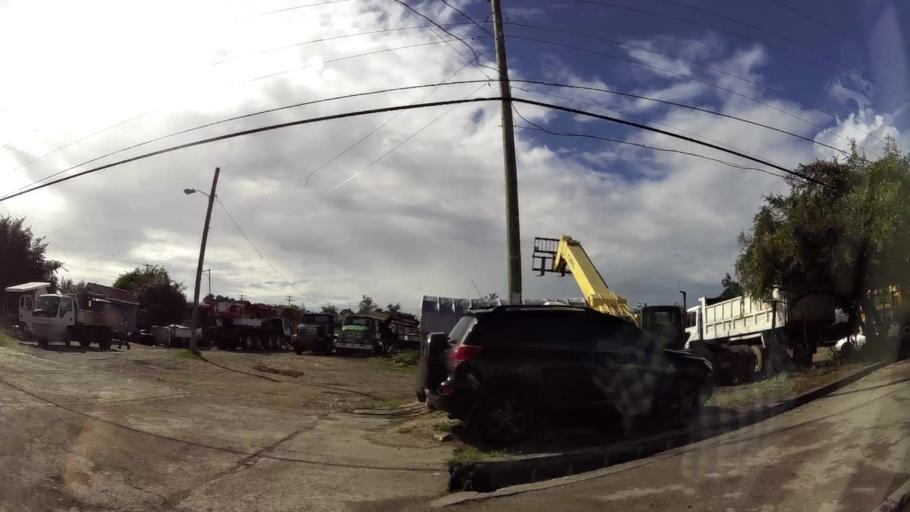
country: AG
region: Saint John
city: Saint John's
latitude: 17.1167
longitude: -61.8284
